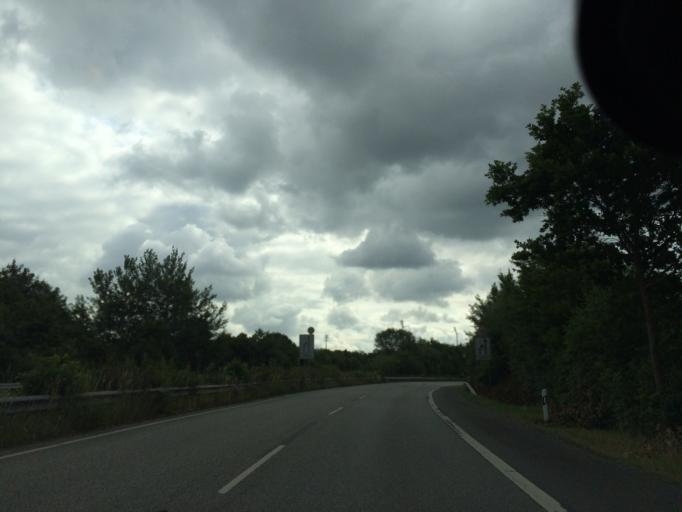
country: DE
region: Schleswig-Holstein
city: Kiel
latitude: 54.3509
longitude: 10.1165
